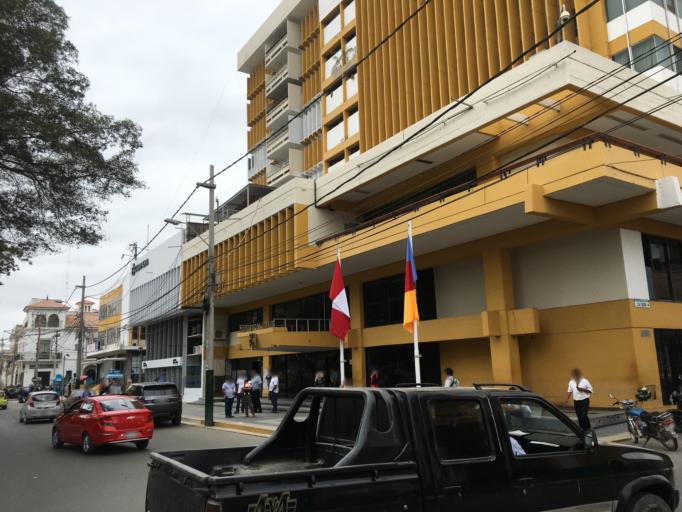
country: PE
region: Piura
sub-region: Provincia de Piura
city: Piura
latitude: -5.1974
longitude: -80.6271
